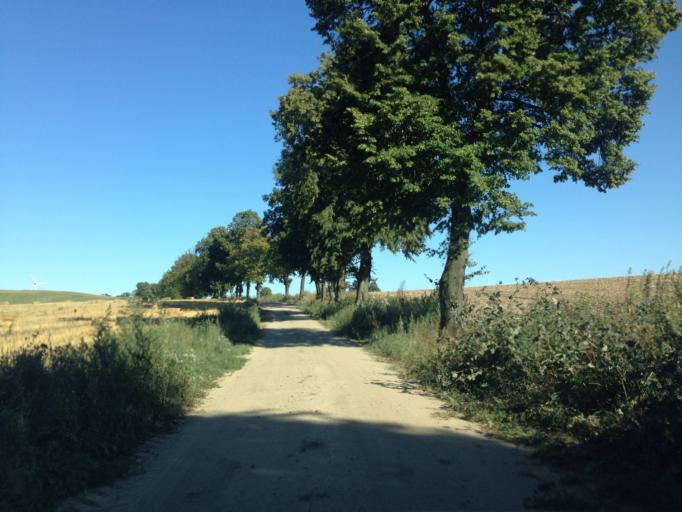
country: PL
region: Kujawsko-Pomorskie
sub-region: Powiat brodnicki
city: Brodnica
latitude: 53.2114
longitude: 19.4697
